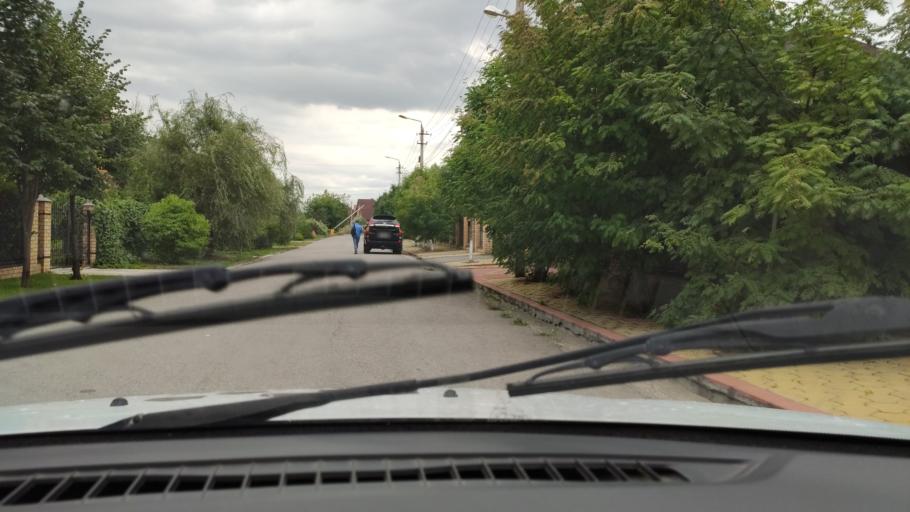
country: RU
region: Perm
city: Kondratovo
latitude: 57.9774
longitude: 56.1119
